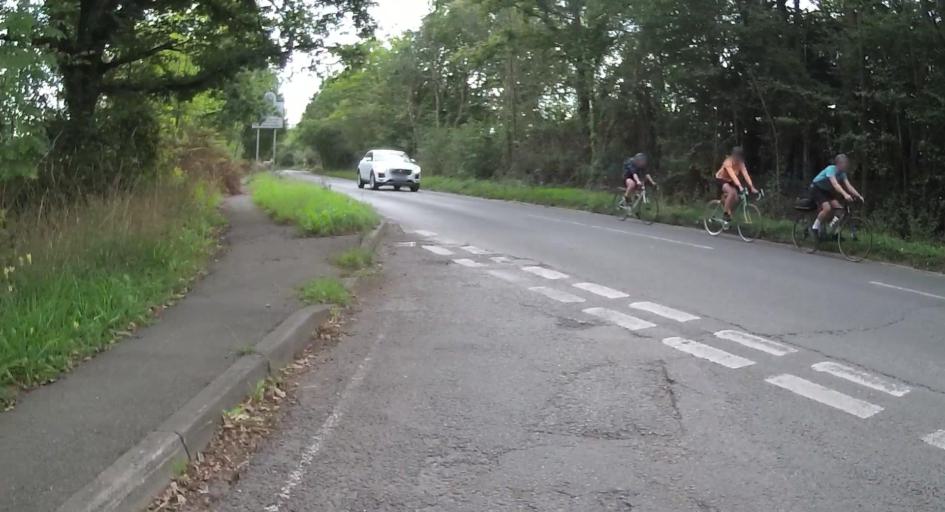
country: GB
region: England
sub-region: Surrey
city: Chobham
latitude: 51.3638
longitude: -0.6096
